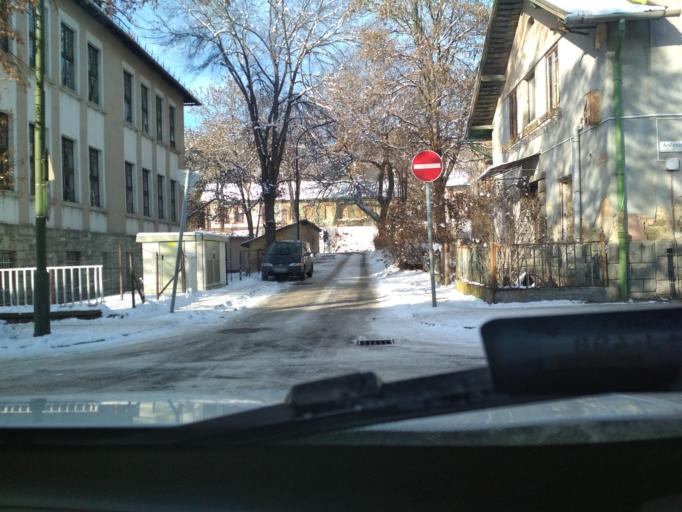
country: HU
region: Nograd
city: Salgotarjan
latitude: 48.1109
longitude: 19.8169
